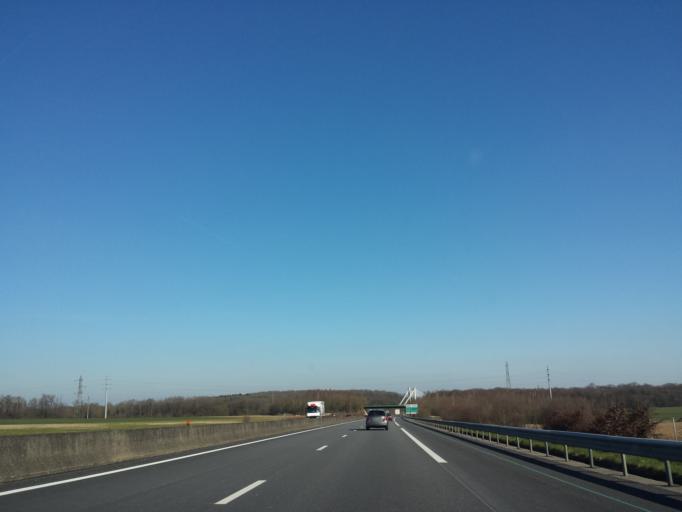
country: FR
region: Picardie
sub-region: Departement de l'Oise
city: Allonne
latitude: 49.3849
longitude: 2.1140
